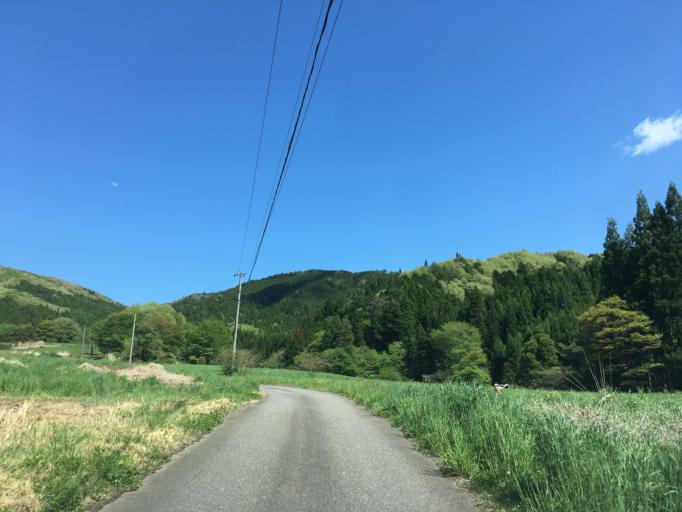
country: JP
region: Fukushima
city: Funehikimachi-funehiki
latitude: 37.3035
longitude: 140.6760
